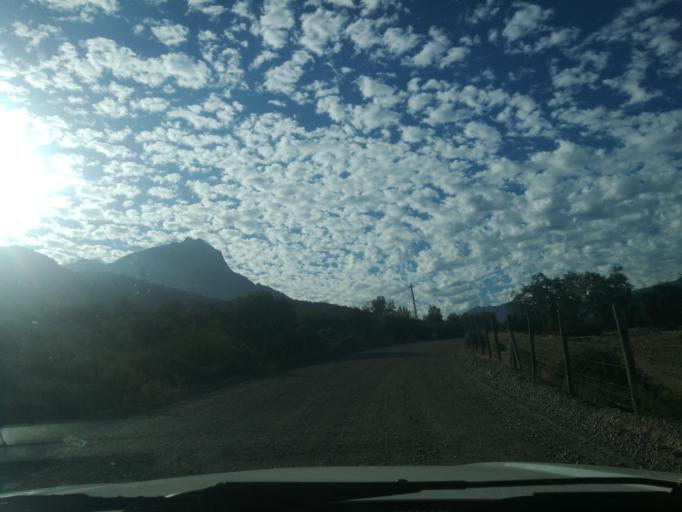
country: CL
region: O'Higgins
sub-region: Provincia de Cachapoal
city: Machali
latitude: -34.2583
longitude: -70.4623
